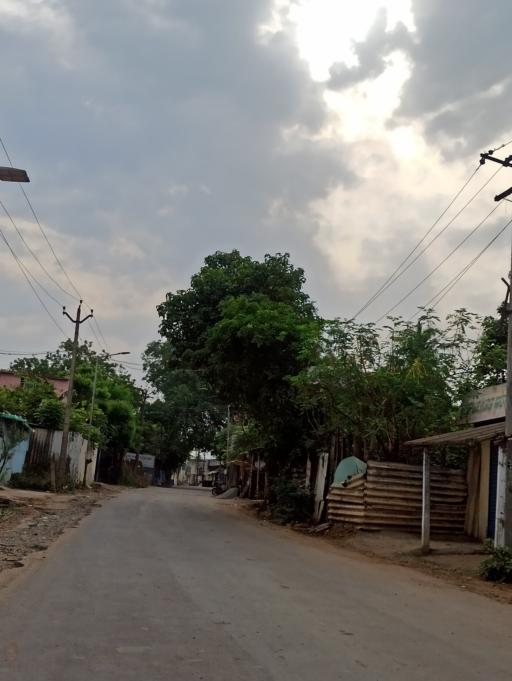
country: IN
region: Tamil Nadu
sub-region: Thiruvallur
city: Chinnasekkadu
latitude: 13.1684
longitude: 80.2323
